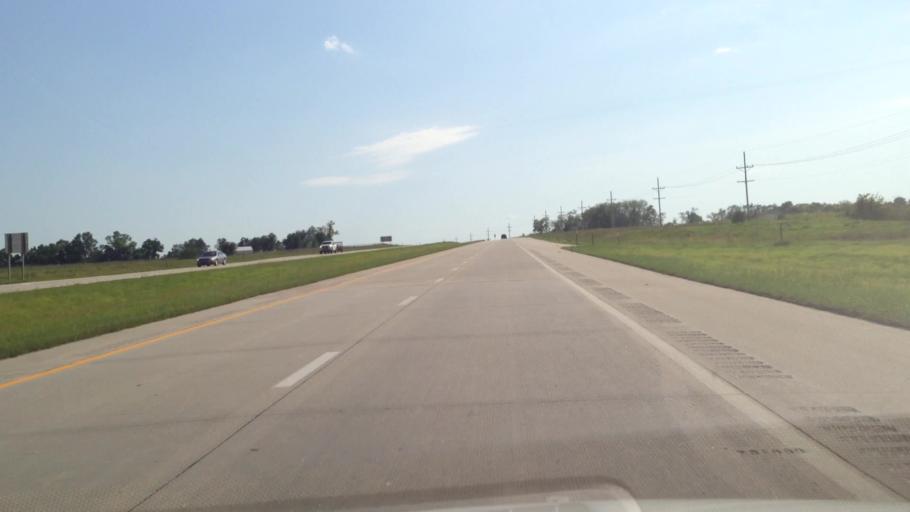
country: US
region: Kansas
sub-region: Linn County
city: Pleasanton
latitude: 38.2167
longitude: -94.7020
